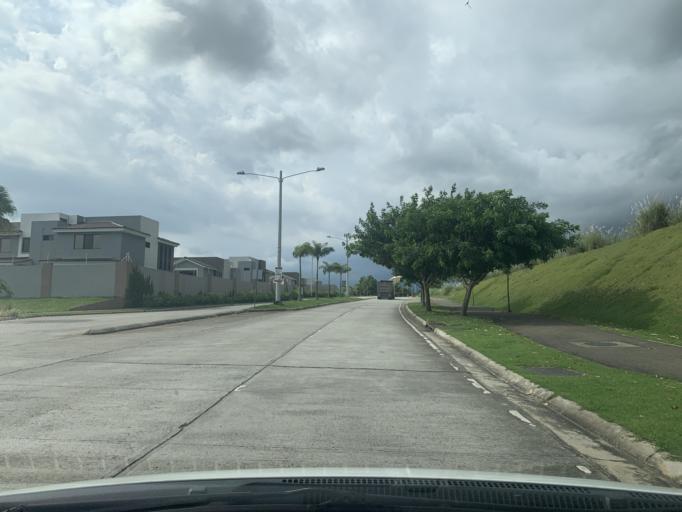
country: PA
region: Panama
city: San Miguelito
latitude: 9.0901
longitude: -79.4673
